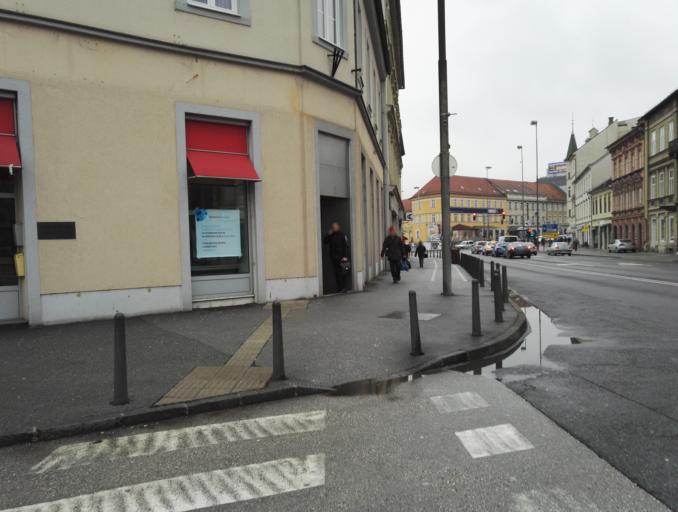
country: SI
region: Maribor
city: Maribor
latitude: 46.5615
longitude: 15.6568
